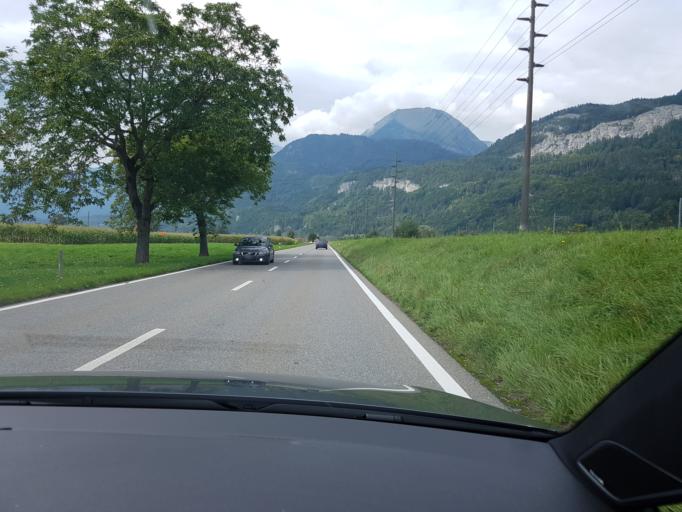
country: CH
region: Bern
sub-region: Interlaken-Oberhasli District
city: Meiringen
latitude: 46.7344
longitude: 8.1583
